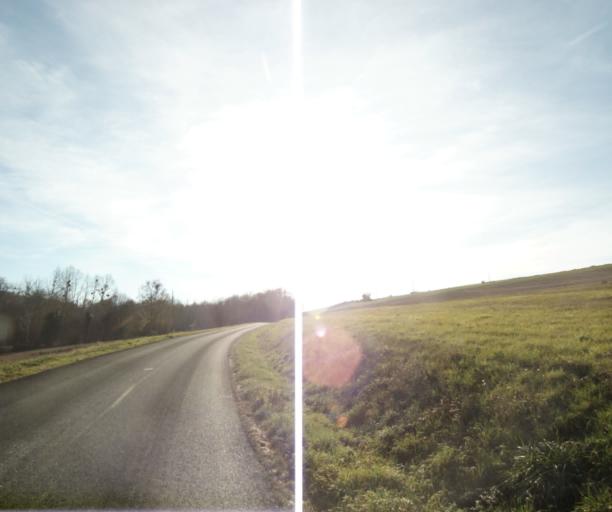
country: FR
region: Poitou-Charentes
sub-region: Departement de la Charente-Maritime
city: Chaniers
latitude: 45.7211
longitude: -0.5212
